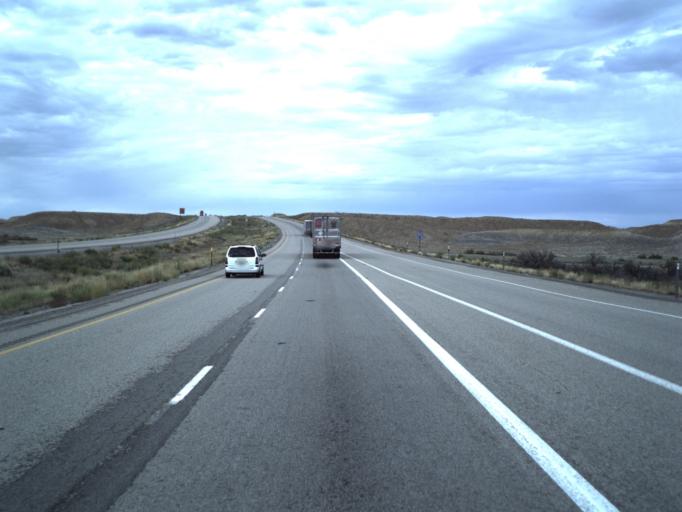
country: US
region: Utah
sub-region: Grand County
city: Moab
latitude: 38.9414
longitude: -109.4024
